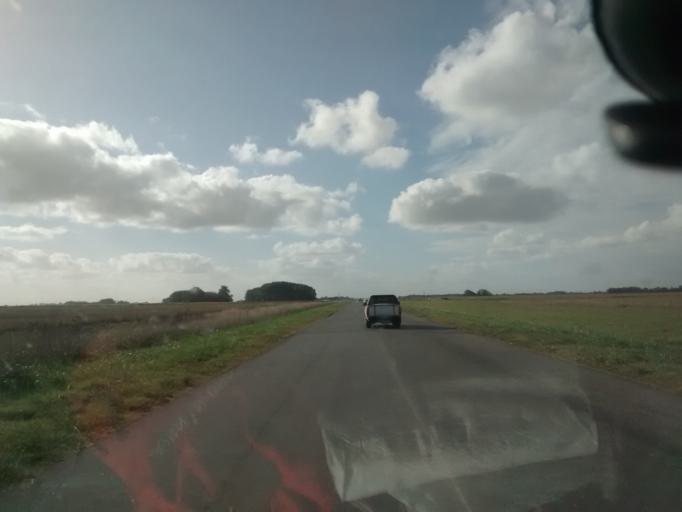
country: AR
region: Buenos Aires
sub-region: Partido de Ayacucho
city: Ayacucho
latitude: -37.2070
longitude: -58.5040
